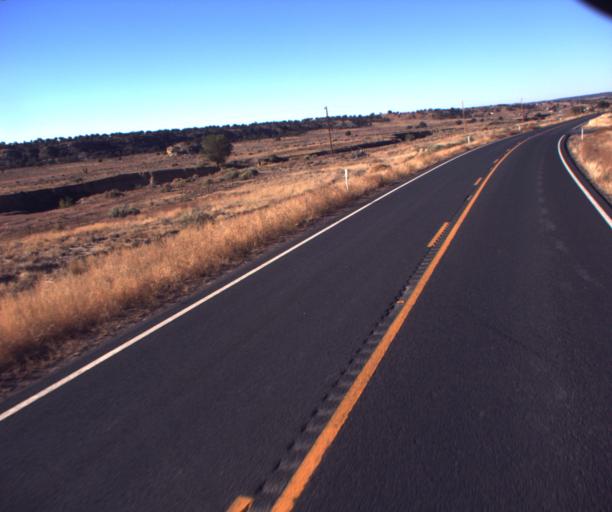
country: US
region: Arizona
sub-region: Apache County
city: Ganado
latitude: 35.7477
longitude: -109.8514
